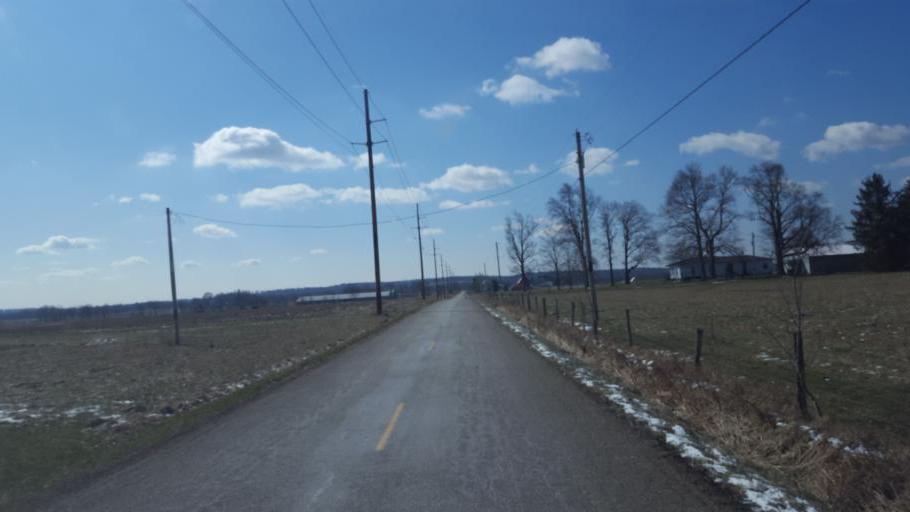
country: US
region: Ohio
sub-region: Licking County
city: Utica
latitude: 40.2795
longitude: -82.4749
